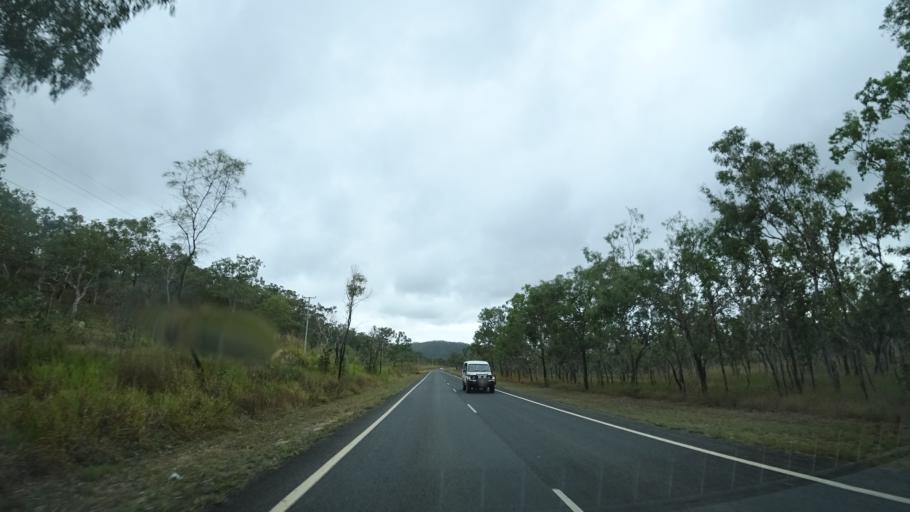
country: AU
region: Queensland
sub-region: Cairns
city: Port Douglas
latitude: -16.7121
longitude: 145.3510
